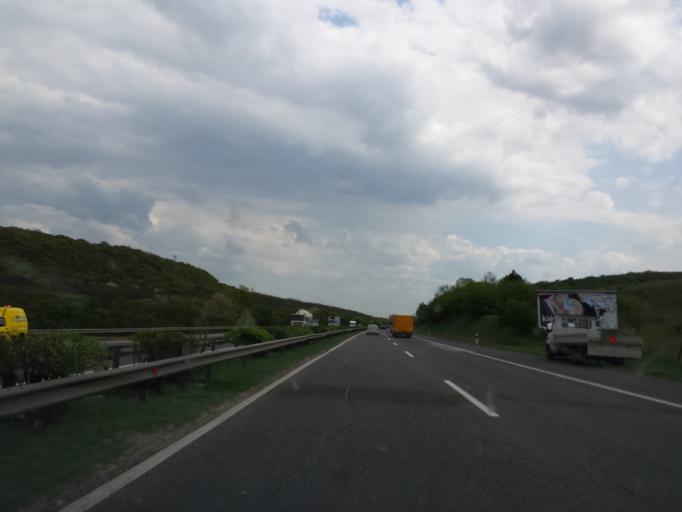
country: HU
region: Fejer
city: Szarliget
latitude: 47.5557
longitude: 18.4875
